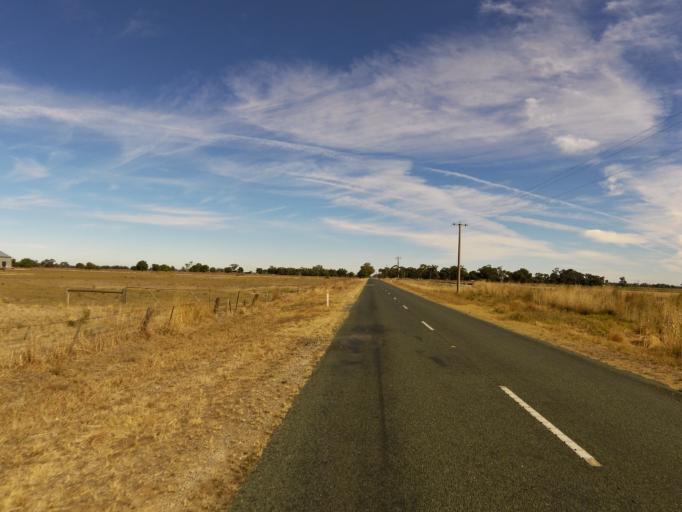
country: AU
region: Victoria
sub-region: Campaspe
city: Echuca
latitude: -36.2991
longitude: 144.4944
